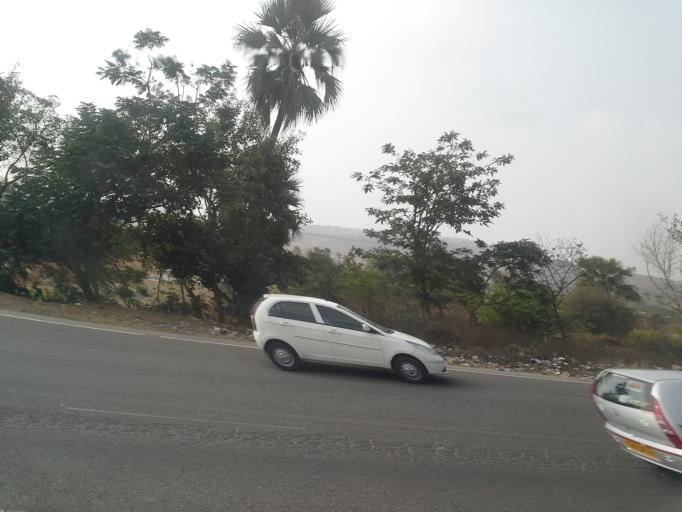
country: IN
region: Telangana
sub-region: Rangareddi
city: Lal Bahadur Nagar
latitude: 17.3124
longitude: 78.6810
